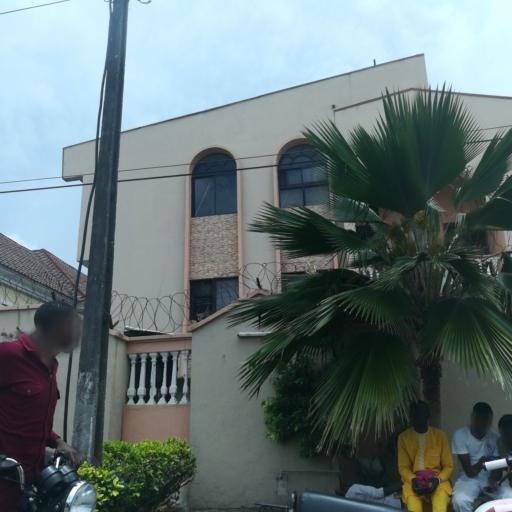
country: NG
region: Lagos
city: Ikoyi
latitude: 6.4391
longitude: 3.4668
